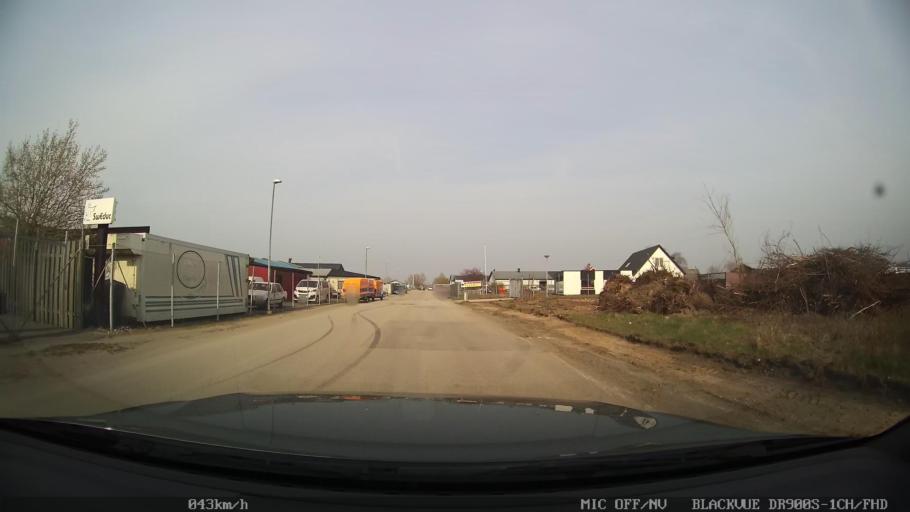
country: SE
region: Skane
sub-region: Ystads Kommun
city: Ystad
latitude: 55.4444
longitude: 13.8495
